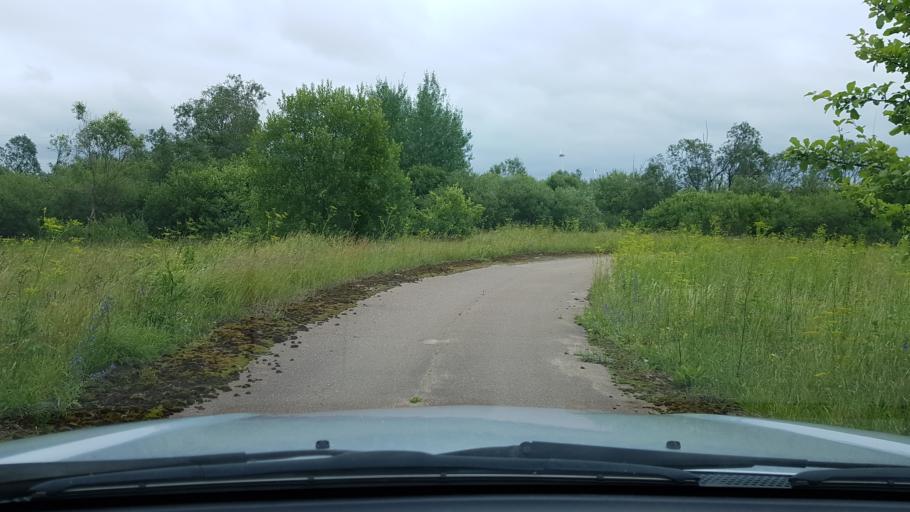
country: EE
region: Ida-Virumaa
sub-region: Narva-Joesuu linn
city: Narva-Joesuu
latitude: 59.3472
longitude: 28.0291
